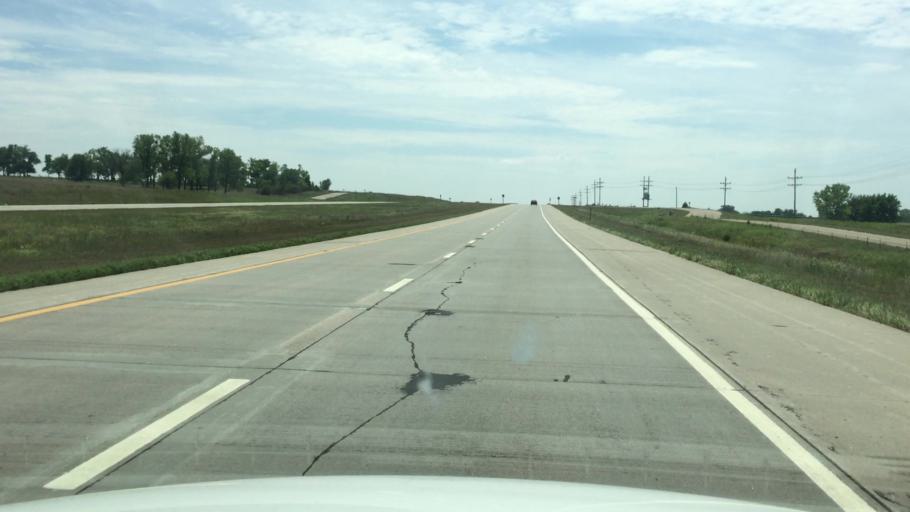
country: US
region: Kansas
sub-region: Shawnee County
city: Silver Lake
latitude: 39.2417
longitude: -95.7196
